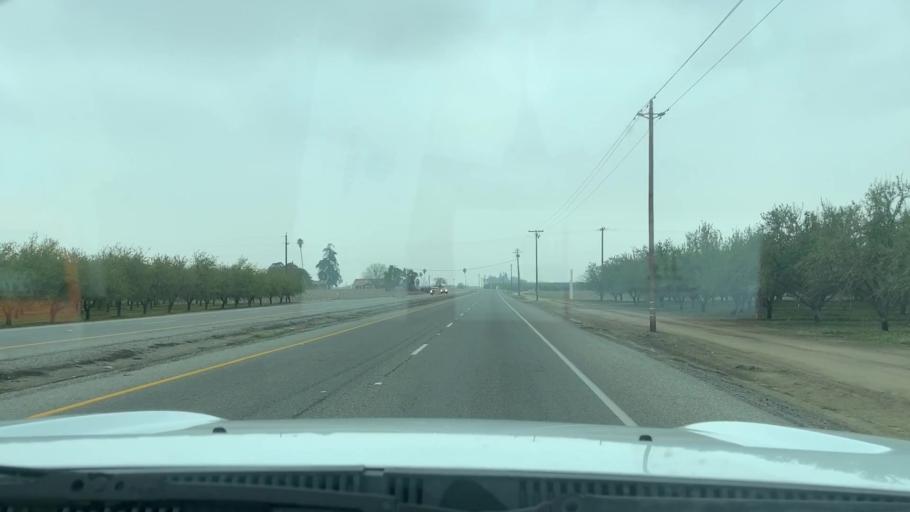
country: US
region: California
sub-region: Kern County
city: Wasco
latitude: 35.5519
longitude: -119.3321
